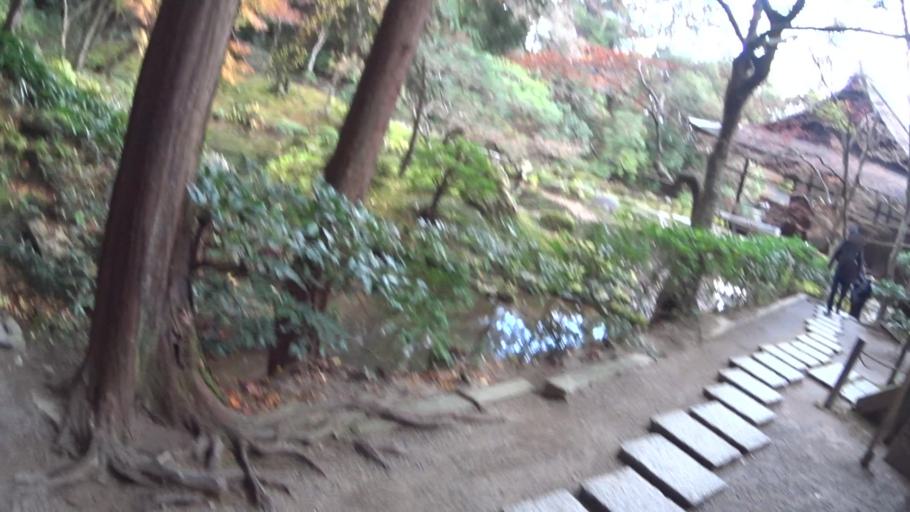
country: JP
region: Kyoto
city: Kyoto
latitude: 35.0093
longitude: 135.7938
